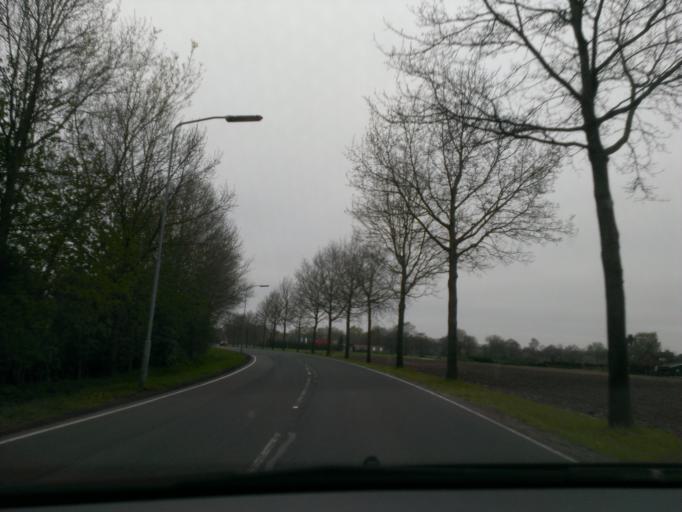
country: NL
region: Gelderland
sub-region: Gemeente Epe
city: Vaassen
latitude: 52.2926
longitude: 5.9826
